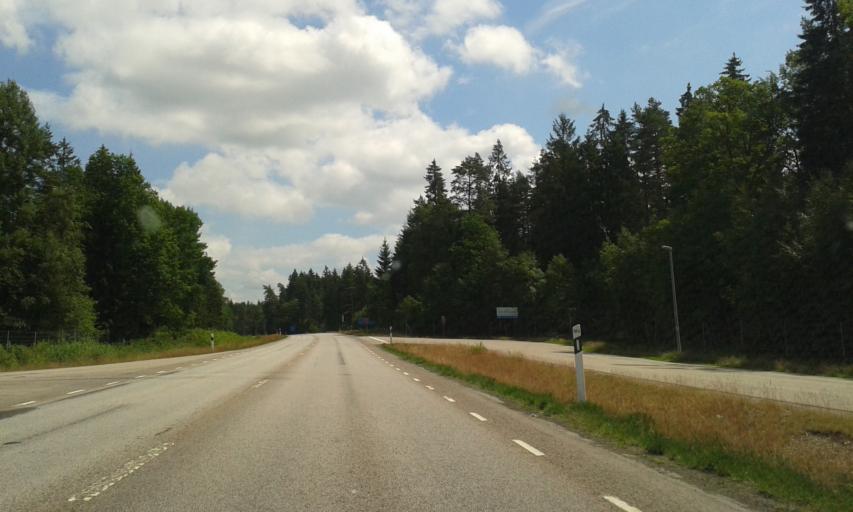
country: SE
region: Kronoberg
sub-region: Alvesta Kommun
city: Alvesta
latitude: 56.9048
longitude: 14.4492
